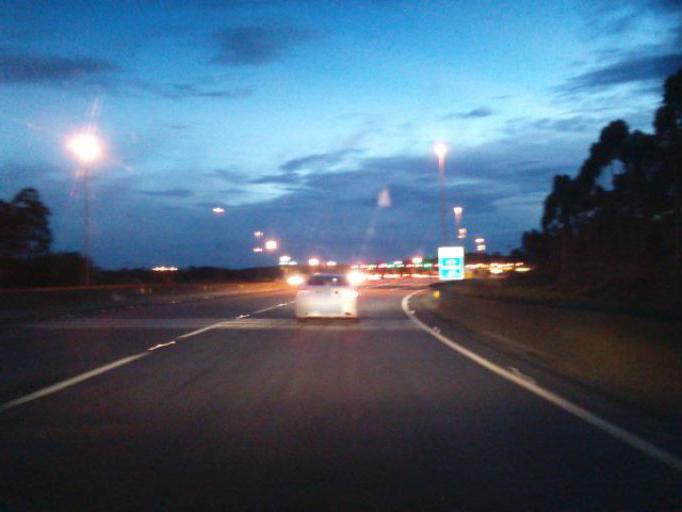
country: BR
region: Santa Catarina
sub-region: Barra Velha
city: Barra Velha
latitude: -26.5885
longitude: -48.7217
